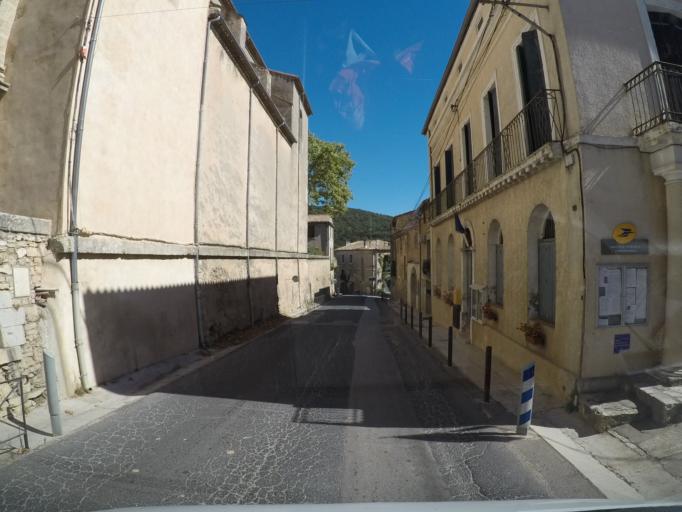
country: FR
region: Languedoc-Roussillon
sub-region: Departement de l'Herault
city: Aniane
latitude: 43.7148
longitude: 3.6173
